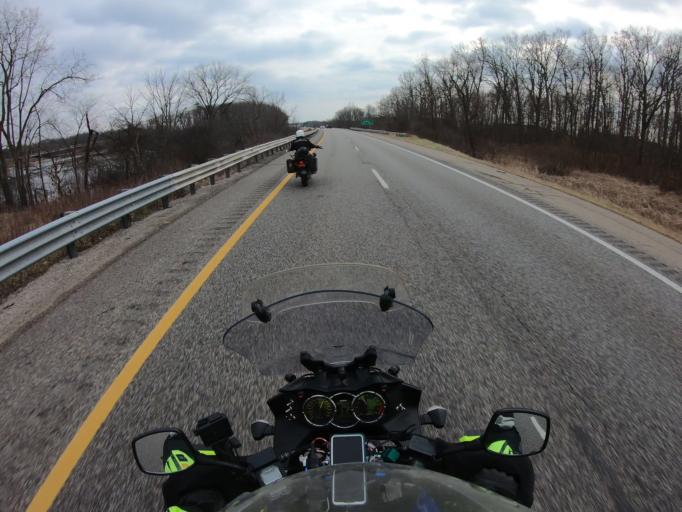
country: US
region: Michigan
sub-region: Genesee County
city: Grand Blanc
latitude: 42.9227
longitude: -83.6855
